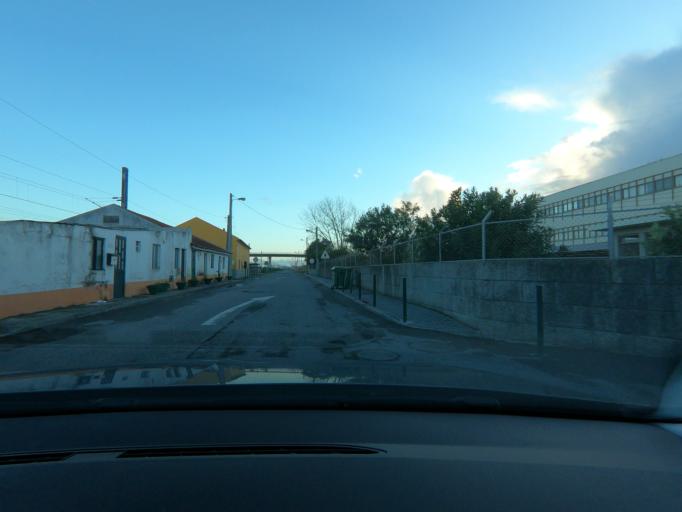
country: PT
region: Lisbon
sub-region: Vila Franca de Xira
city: Castanheira do Ribatejo
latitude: 39.0041
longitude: -8.9551
